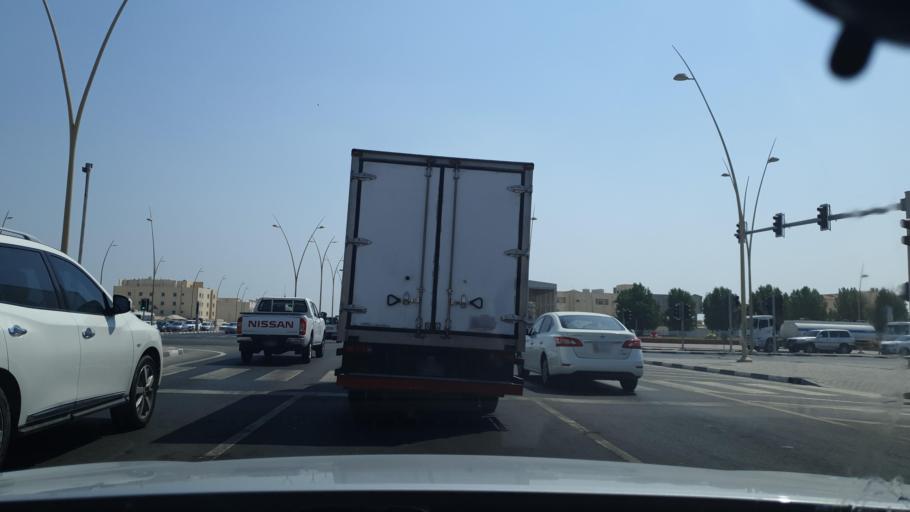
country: QA
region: Al Khawr
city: Al Khawr
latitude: 25.6808
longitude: 51.4966
